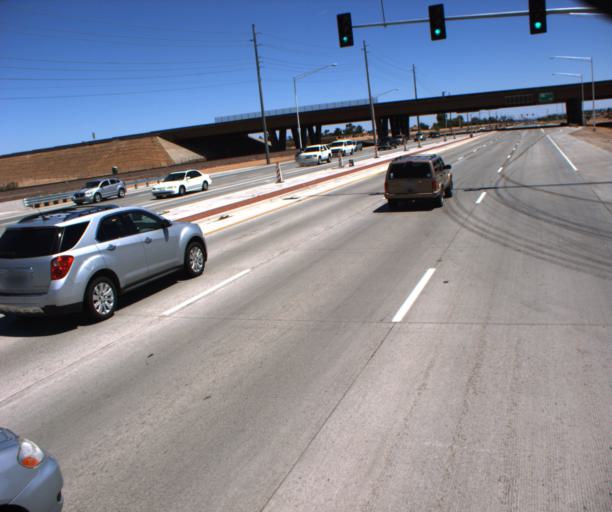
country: US
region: Arizona
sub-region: Maricopa County
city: Sun City West
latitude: 33.6817
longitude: -112.4056
